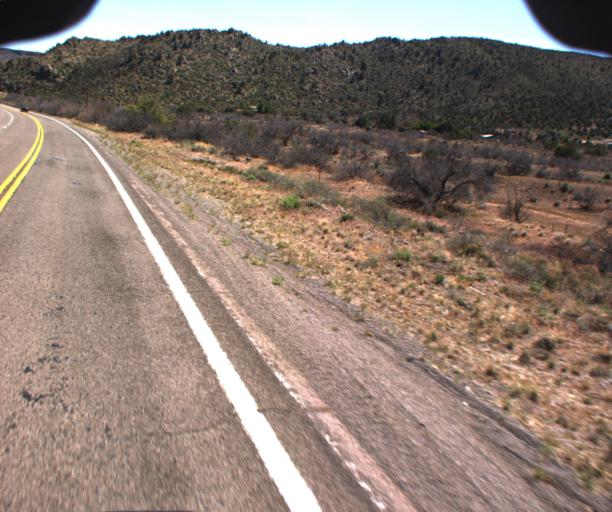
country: US
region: Arizona
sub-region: Mohave County
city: Peach Springs
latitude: 35.4255
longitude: -113.6495
